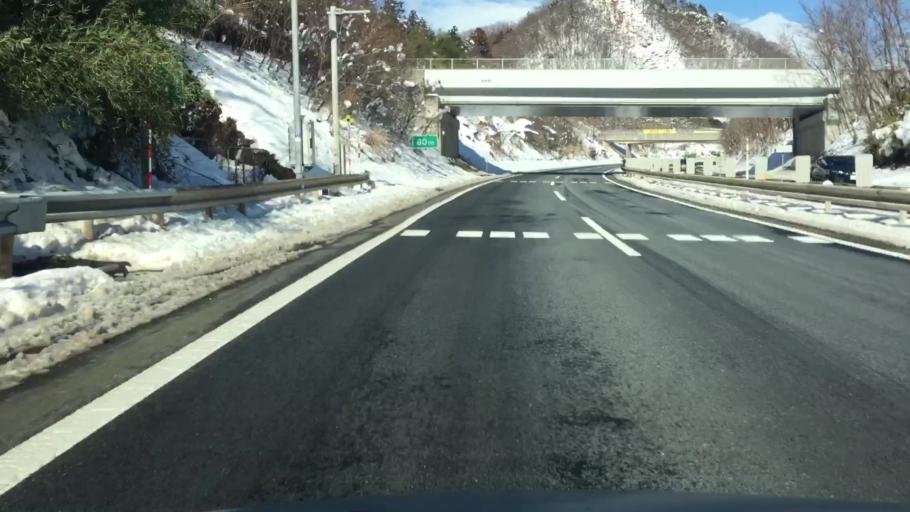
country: JP
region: Gunma
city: Numata
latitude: 36.7132
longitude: 138.9757
